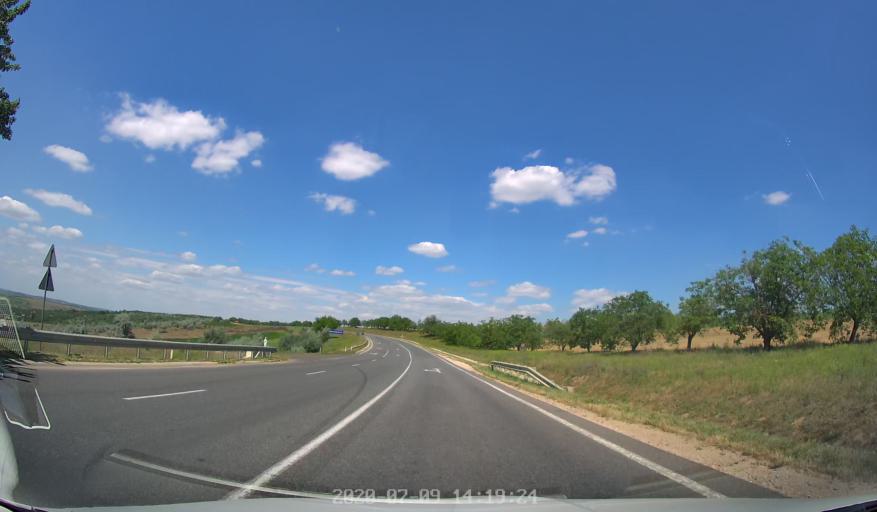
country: MD
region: Rezina
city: Saharna
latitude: 47.5992
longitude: 28.8310
